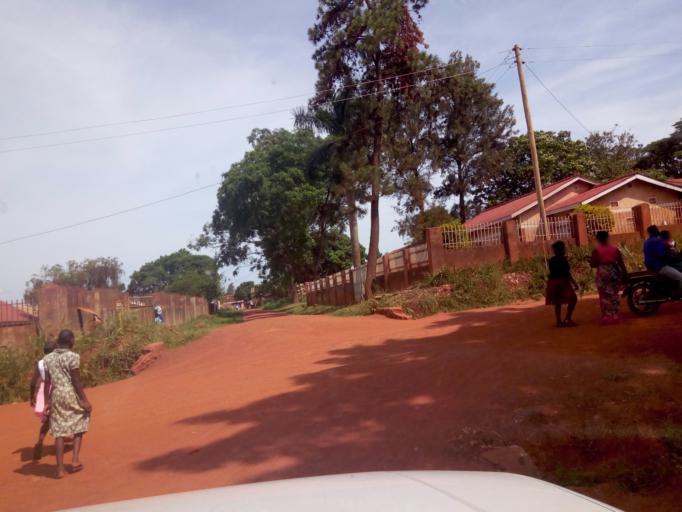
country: UG
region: Western Region
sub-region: Masindi District
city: Masindi
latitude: 1.6794
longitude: 31.7197
